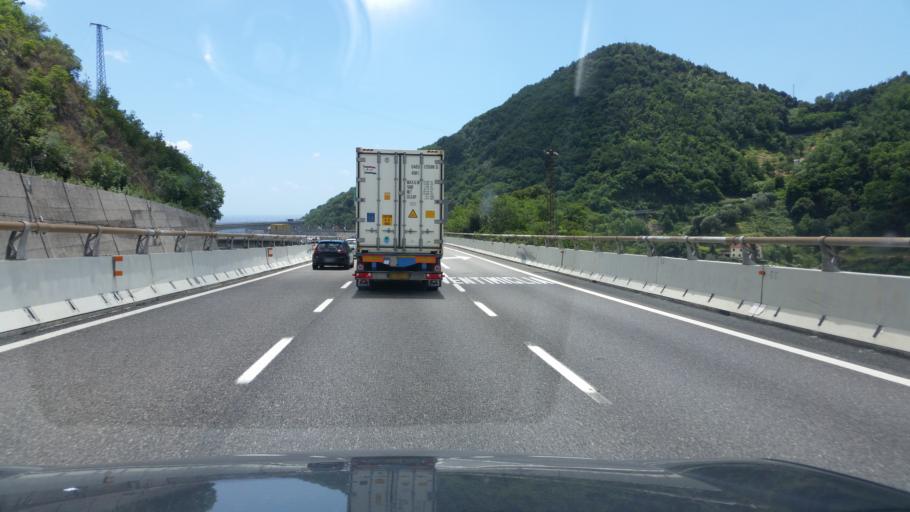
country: IT
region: Liguria
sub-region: Provincia di Genova
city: Mele
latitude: 44.4368
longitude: 8.7376
